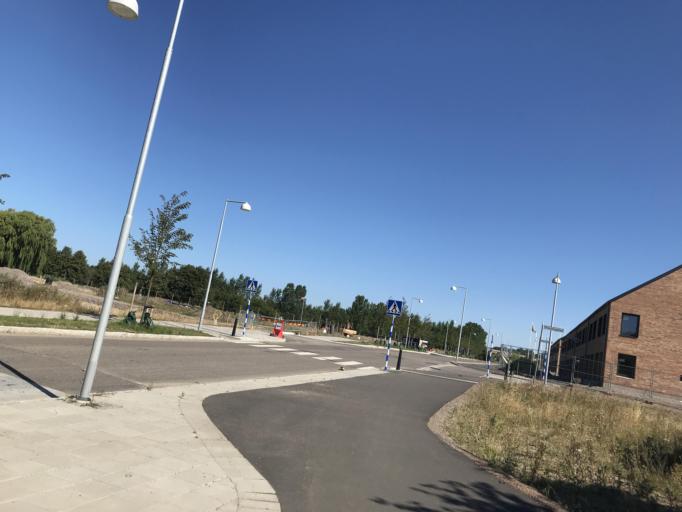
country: SE
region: Skane
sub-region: Landskrona
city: Landskrona
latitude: 55.9017
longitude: 12.8142
